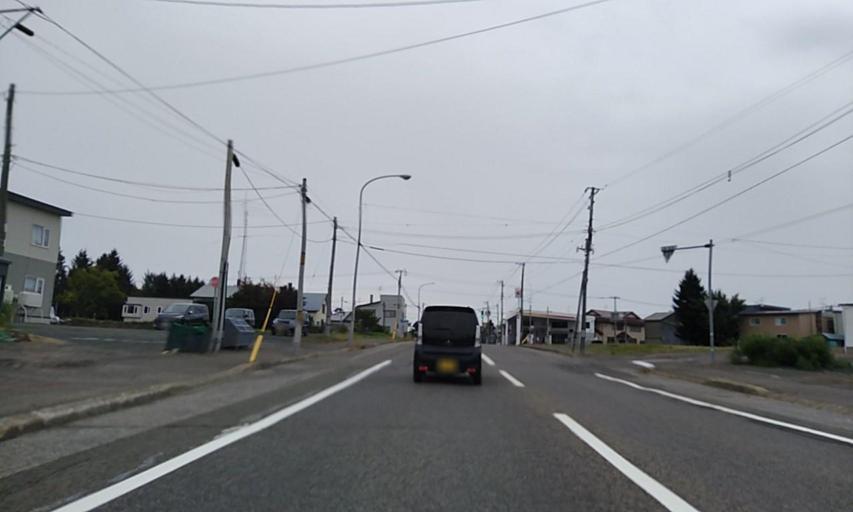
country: JP
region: Hokkaido
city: Bihoro
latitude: 43.9136
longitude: 144.1696
